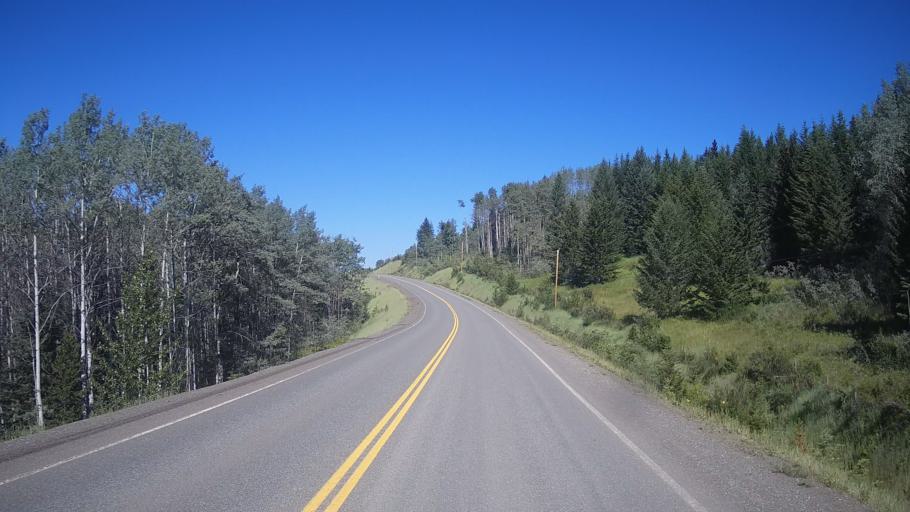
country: CA
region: British Columbia
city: Kamloops
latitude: 51.4952
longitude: -120.5758
